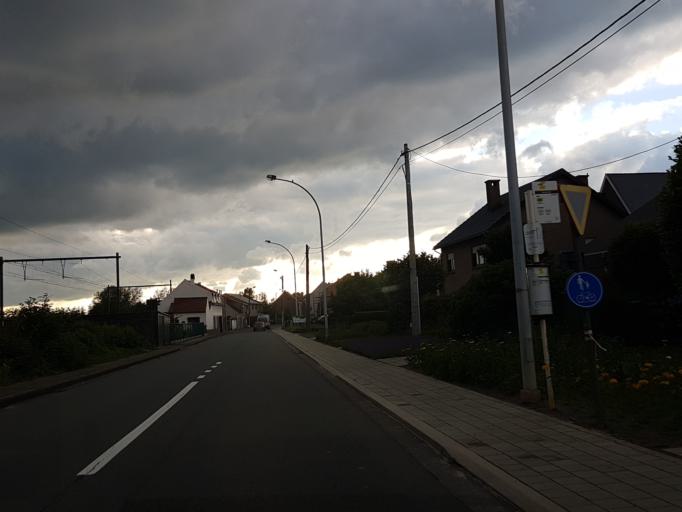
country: BE
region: Flanders
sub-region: Provincie Vlaams-Brabant
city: Opwijk
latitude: 50.9782
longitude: 4.1784
